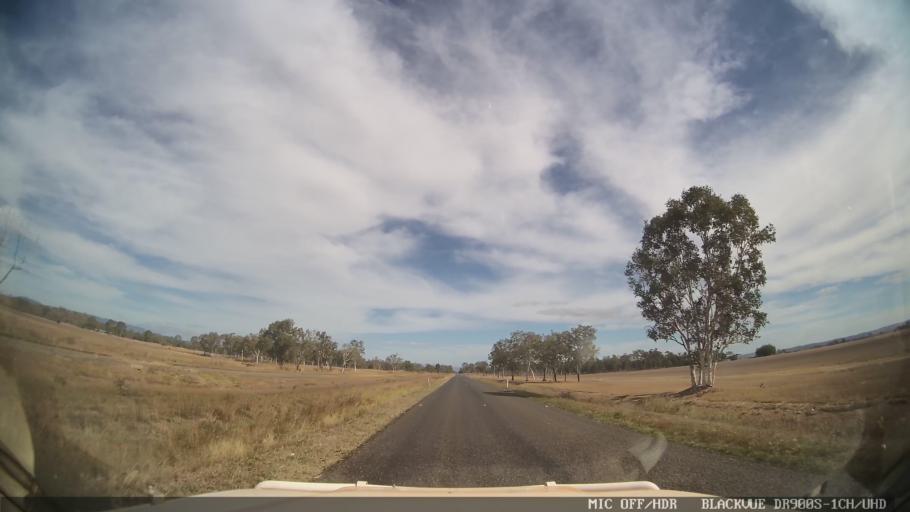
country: AU
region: Queensland
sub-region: Tablelands
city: Mareeba
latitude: -16.9314
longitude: 145.4180
